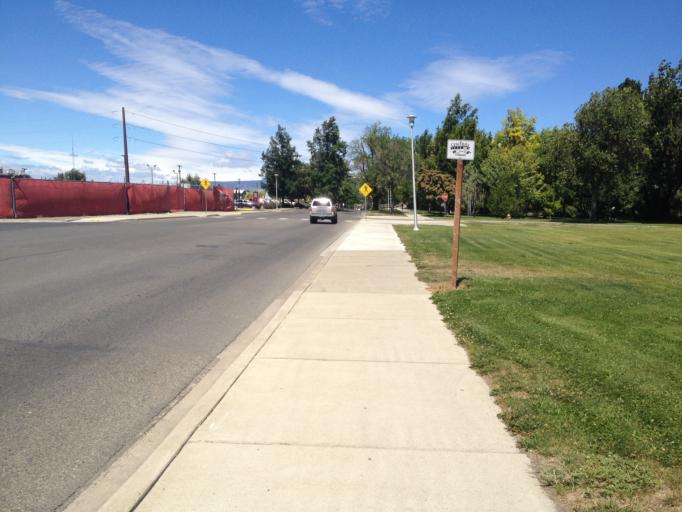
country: US
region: Washington
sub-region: Kittitas County
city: Ellensburg
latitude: 47.0034
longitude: -120.5432
